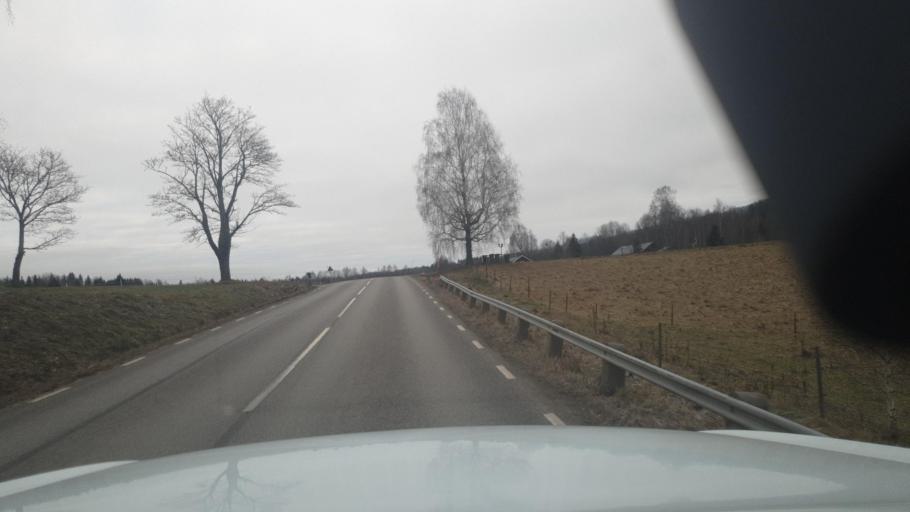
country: SE
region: Vaermland
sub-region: Sunne Kommun
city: Sunne
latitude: 59.8120
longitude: 13.0269
